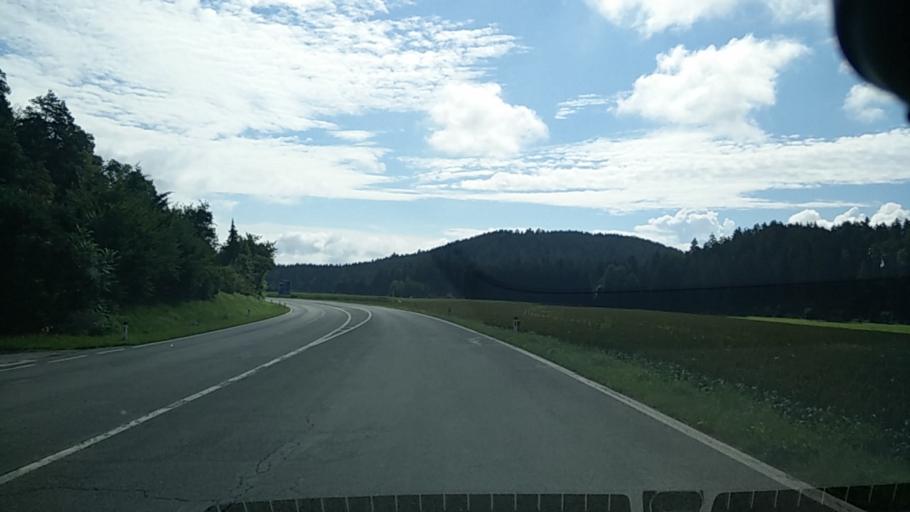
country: AT
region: Carinthia
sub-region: Politischer Bezirk Volkermarkt
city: Voelkermarkt
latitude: 46.6533
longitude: 14.5558
